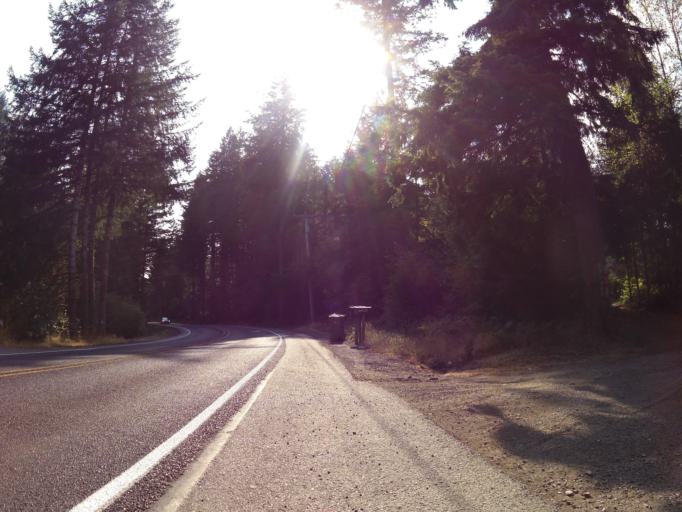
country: US
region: Washington
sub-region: Mason County
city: Belfair
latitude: 47.5235
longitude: -122.7710
